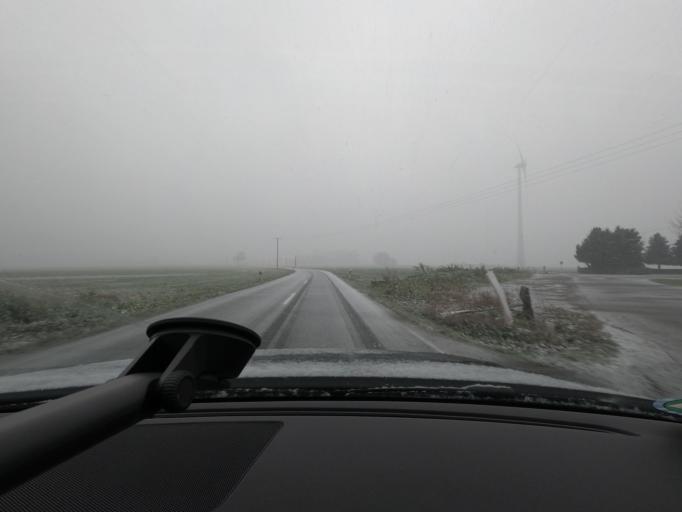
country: DE
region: North Rhine-Westphalia
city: Marsberg
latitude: 51.5306
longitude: 8.8428
